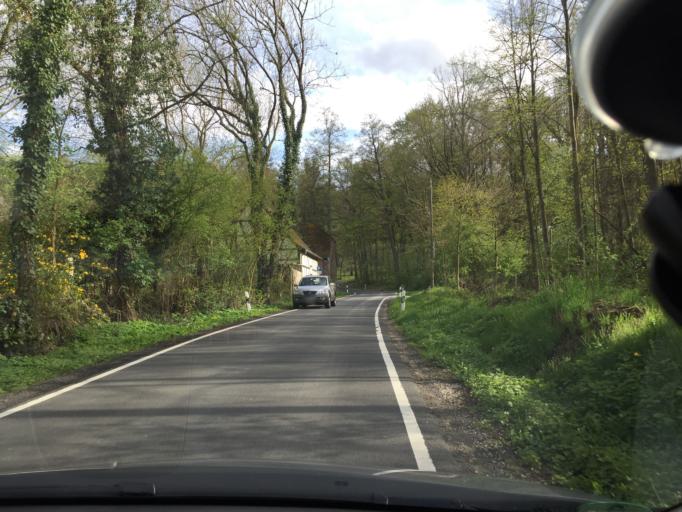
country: DE
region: Bavaria
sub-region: Regierungsbezirk Unterfranken
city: Goldbach
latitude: 49.9812
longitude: 9.1771
